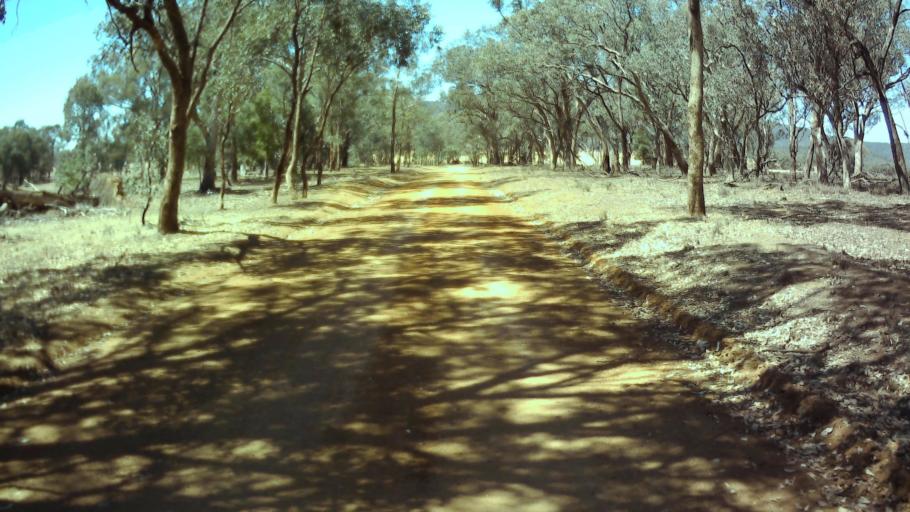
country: AU
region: New South Wales
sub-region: Weddin
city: Grenfell
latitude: -33.9537
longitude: 148.0846
